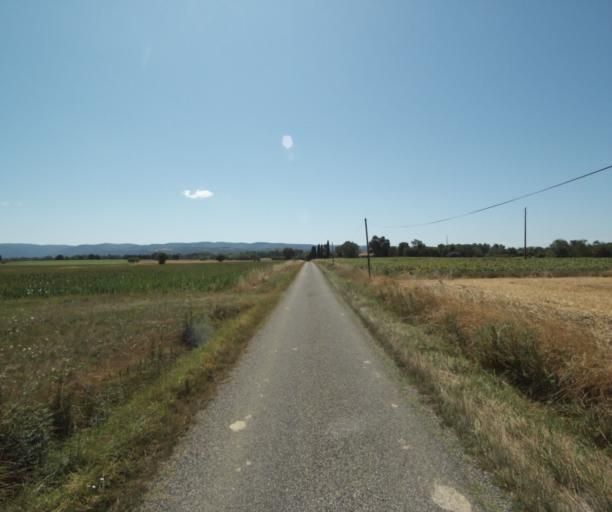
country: FR
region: Midi-Pyrenees
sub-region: Departement de la Haute-Garonne
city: Revel
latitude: 43.4774
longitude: 1.9582
